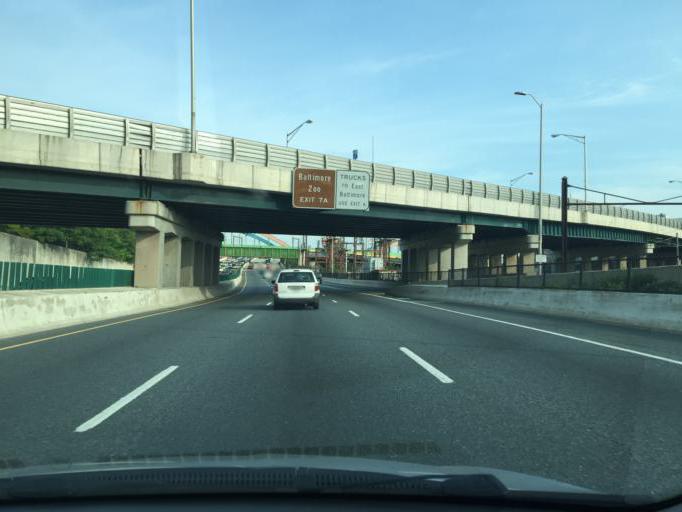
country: US
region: Maryland
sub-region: City of Baltimore
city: Baltimore
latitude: 39.3076
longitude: -76.6173
